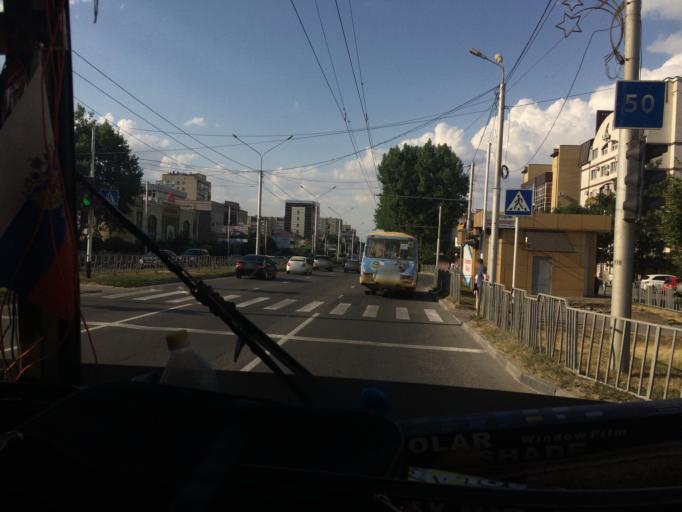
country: RU
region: Stavropol'skiy
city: Stavropol'
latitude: 45.0152
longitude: 41.9313
